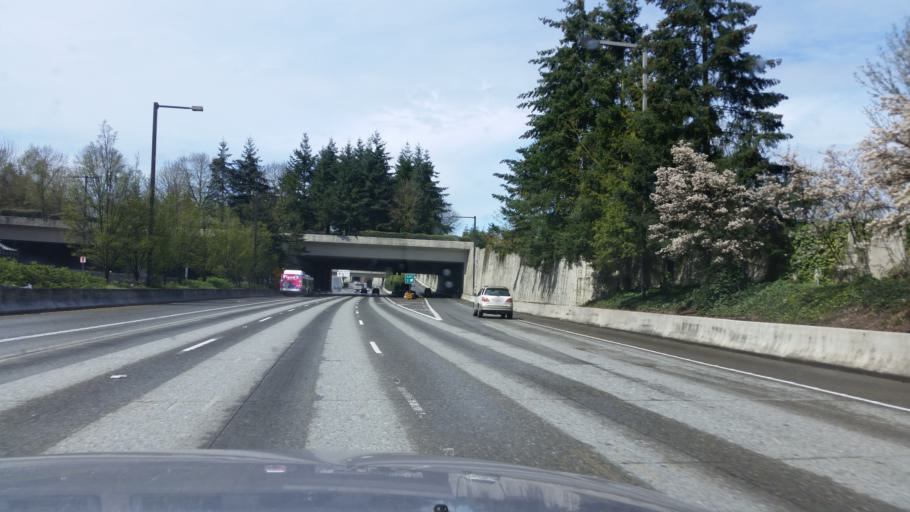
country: US
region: Washington
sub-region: King County
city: Mercer Island
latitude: 47.5849
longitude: -122.2252
